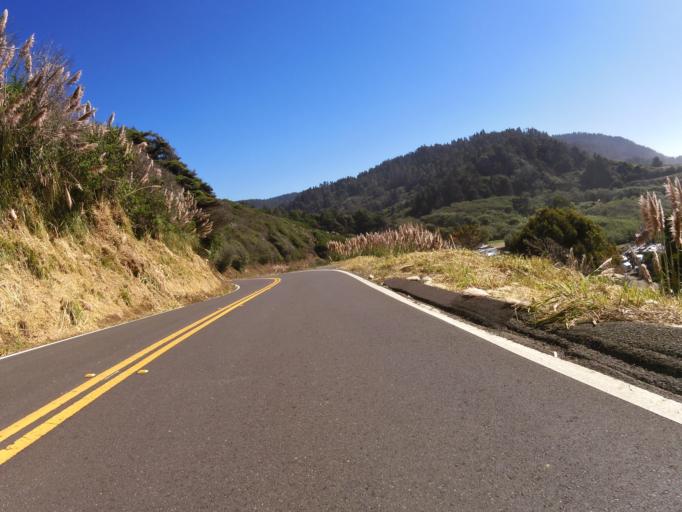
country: US
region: California
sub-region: Mendocino County
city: Fort Bragg
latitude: 39.6520
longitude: -123.7829
